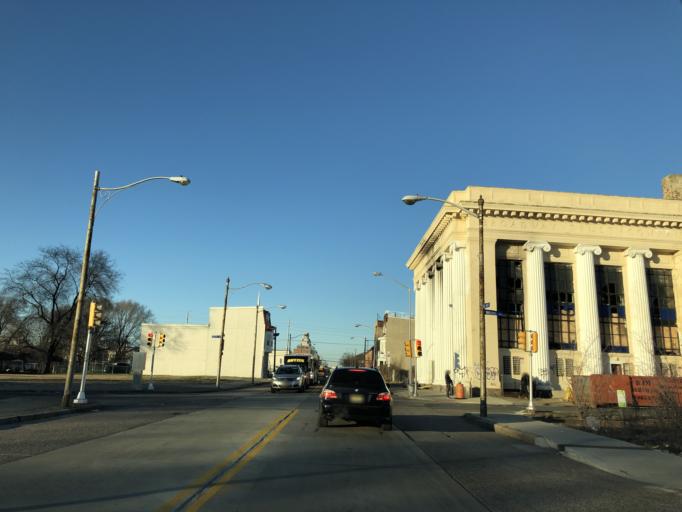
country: US
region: New Jersey
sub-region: Camden County
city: Camden
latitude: 39.9334
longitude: -75.1195
